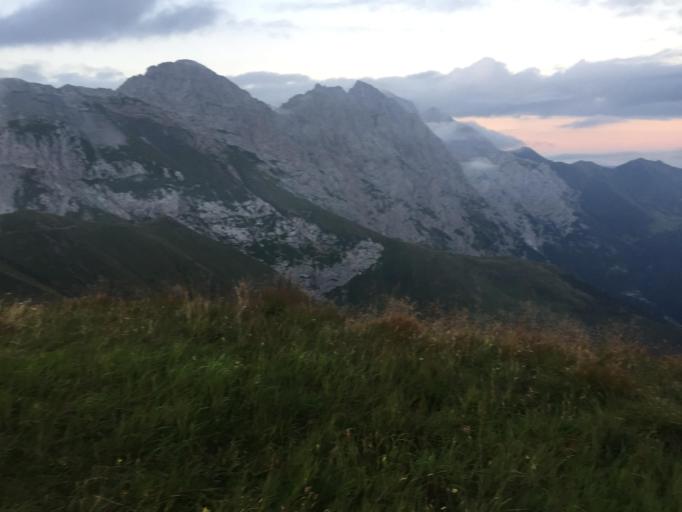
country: IT
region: Friuli Venezia Giulia
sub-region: Provincia di Udine
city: Forni Avoltri
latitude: 46.6001
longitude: 12.8193
